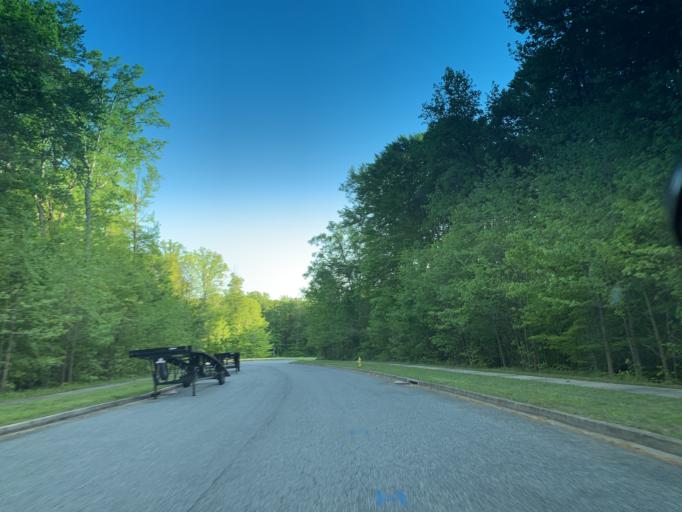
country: US
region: Maryland
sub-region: Harford County
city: Aberdeen
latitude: 39.5227
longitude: -76.2006
